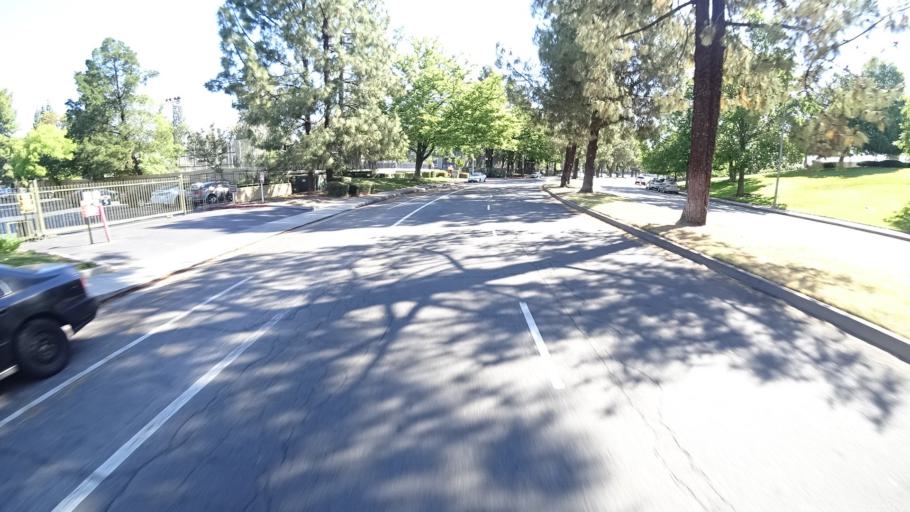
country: US
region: California
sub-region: Sacramento County
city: Arden-Arcade
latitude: 38.5971
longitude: -121.4339
